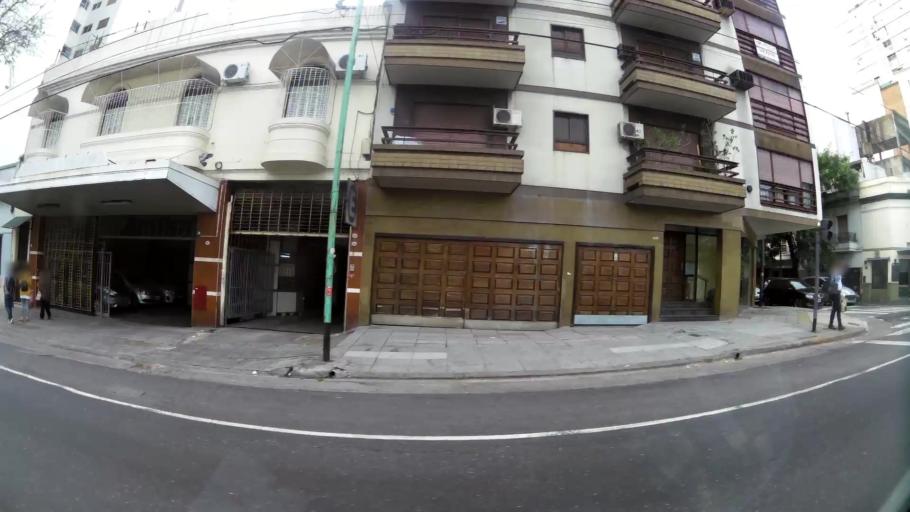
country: AR
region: Buenos Aires F.D.
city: Villa Santa Rita
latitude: -34.6326
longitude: -58.4579
